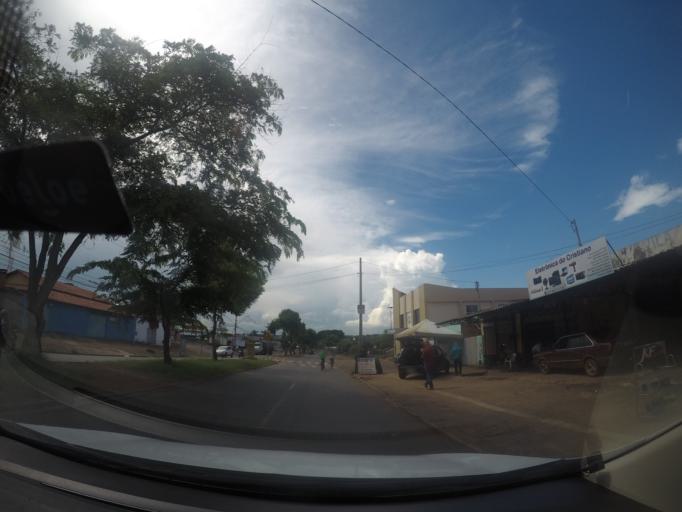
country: BR
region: Goias
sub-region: Trindade
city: Trindade
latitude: -16.6814
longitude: -49.3858
